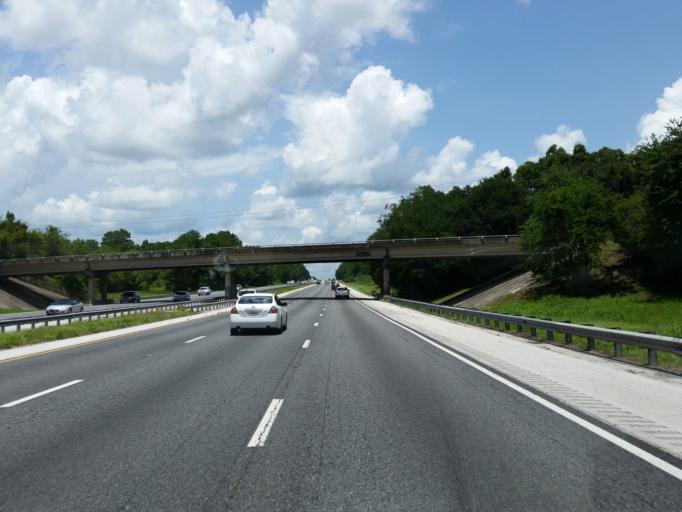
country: US
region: Florida
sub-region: Marion County
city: Citra
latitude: 29.3660
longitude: -82.2259
